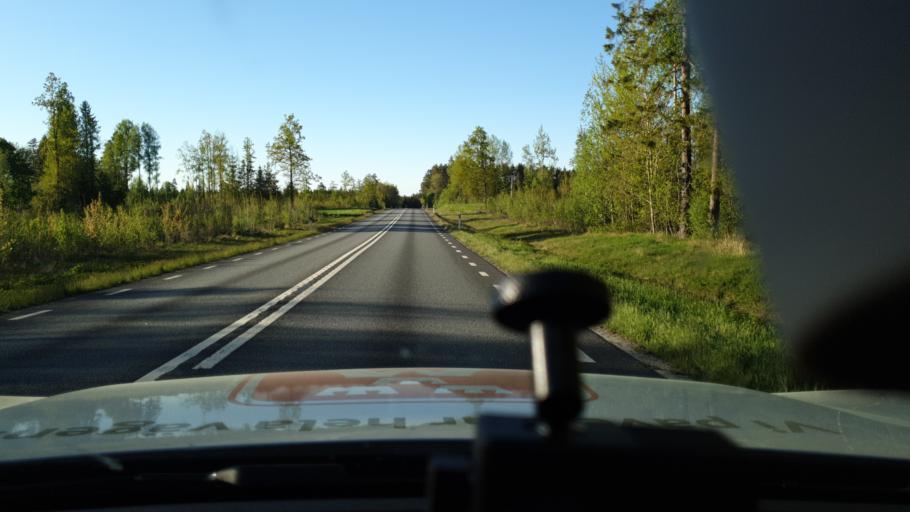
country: SE
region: Joenkoeping
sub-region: Vetlanda Kommun
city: Ekenassjon
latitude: 57.5225
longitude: 14.9886
